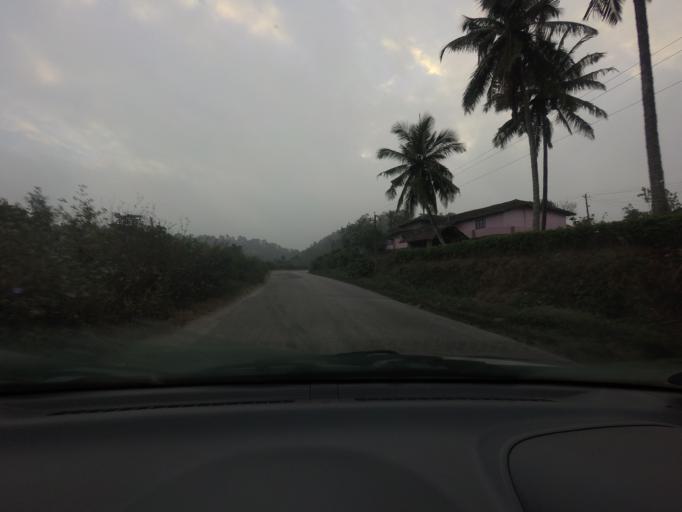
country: IN
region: Karnataka
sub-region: Hassan
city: Sakleshpur
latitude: 12.9185
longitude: 75.7538
